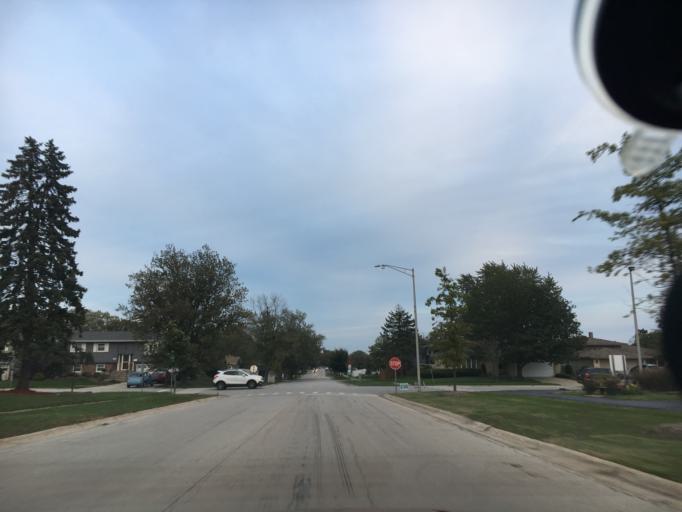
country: US
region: Illinois
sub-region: Cook County
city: Oak Forest
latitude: 41.6098
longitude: -87.7764
